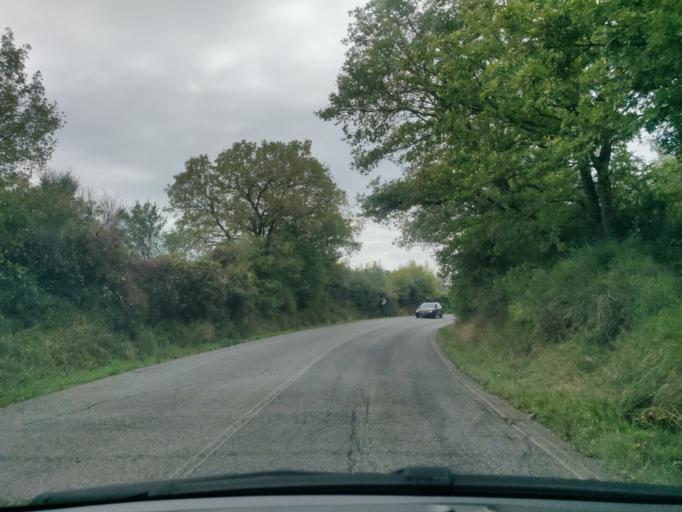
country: IT
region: Latium
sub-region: Citta metropolitana di Roma Capitale
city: Allumiere
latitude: 42.1328
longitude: 11.8696
